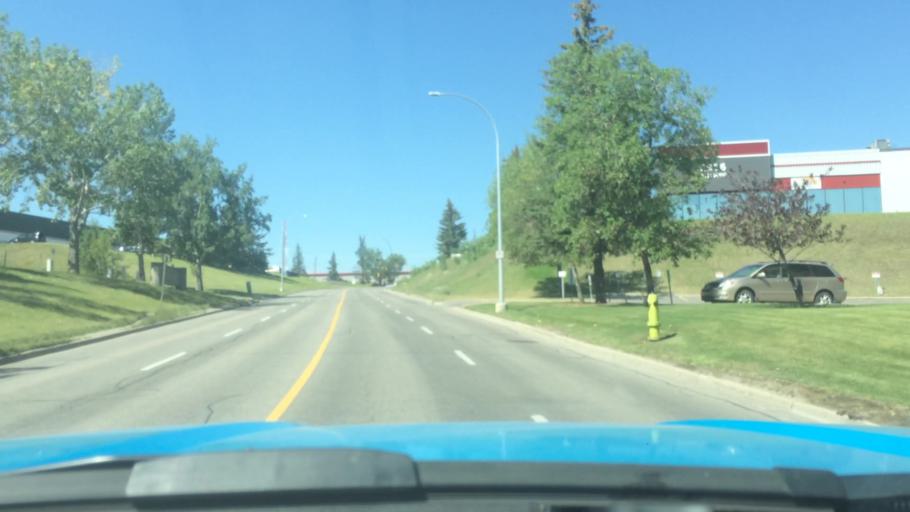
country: CA
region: Alberta
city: Calgary
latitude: 51.0570
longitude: -113.9900
